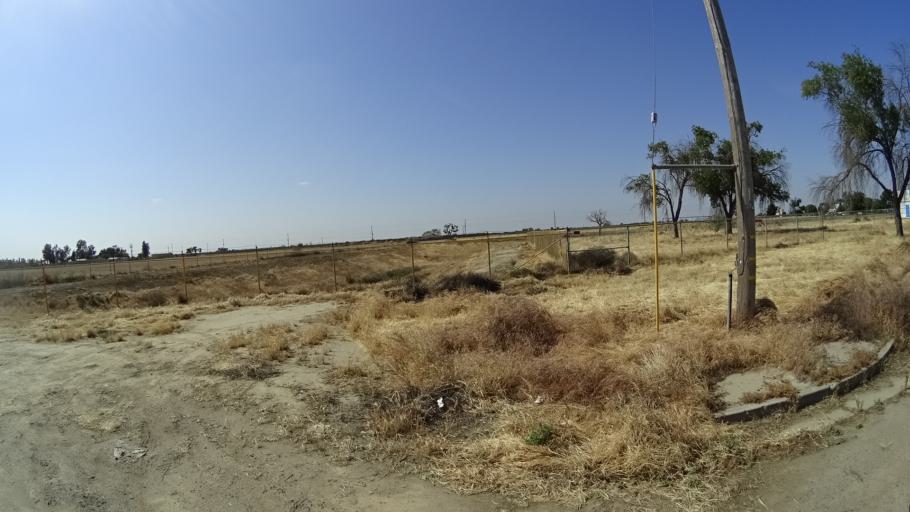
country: US
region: California
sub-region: Kings County
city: Home Garden
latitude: 36.3018
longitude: -119.6284
